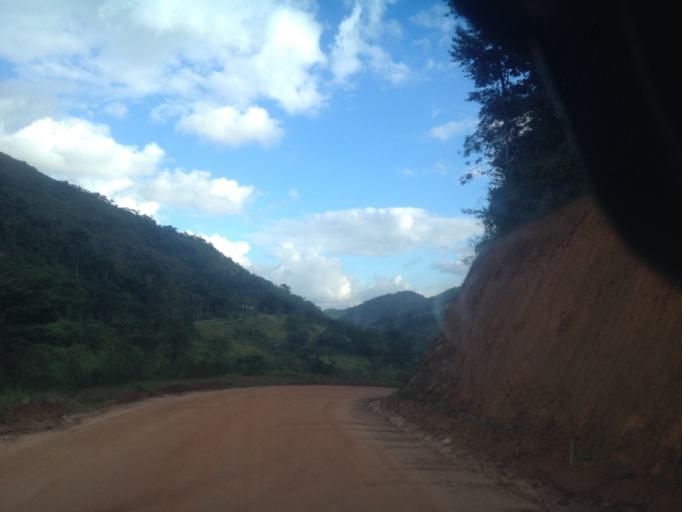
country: BR
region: Rio de Janeiro
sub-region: Quatis
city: Quatis
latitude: -22.2377
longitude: -44.2619
